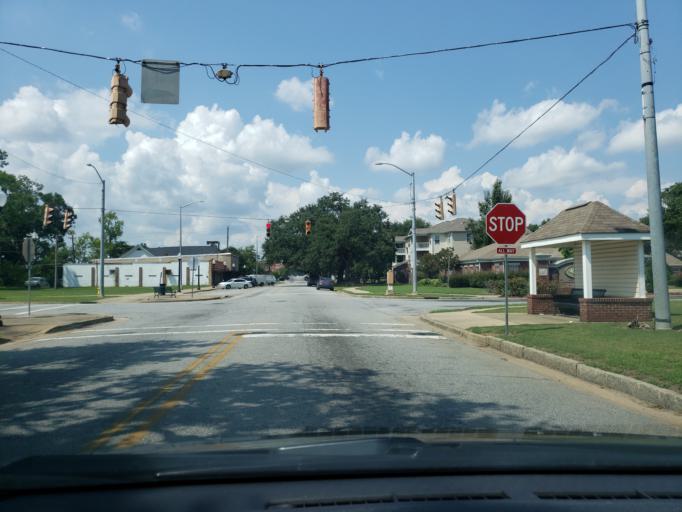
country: US
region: Georgia
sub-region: Dougherty County
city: Albany
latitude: 31.5720
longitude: -84.1536
